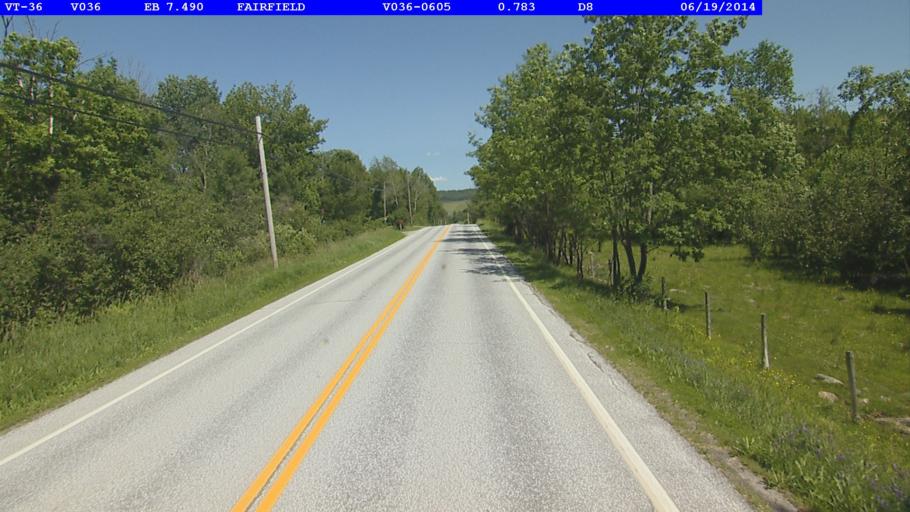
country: US
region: Vermont
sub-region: Franklin County
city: Saint Albans
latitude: 44.7884
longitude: -73.0161
